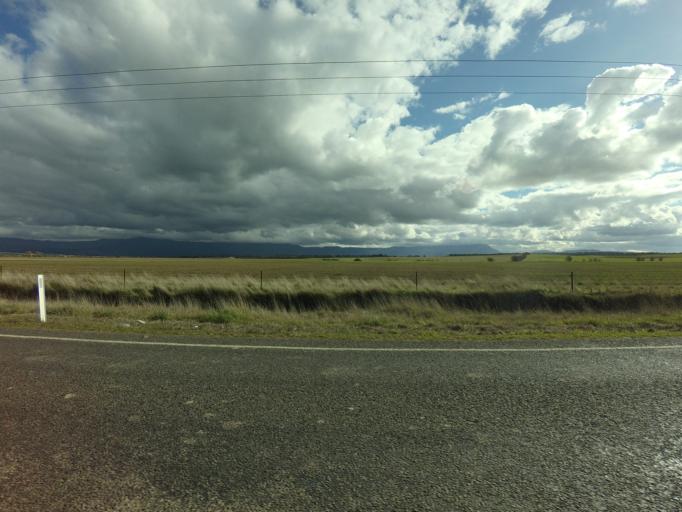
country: AU
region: Tasmania
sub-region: Northern Midlands
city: Longford
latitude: -41.7068
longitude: 147.0792
